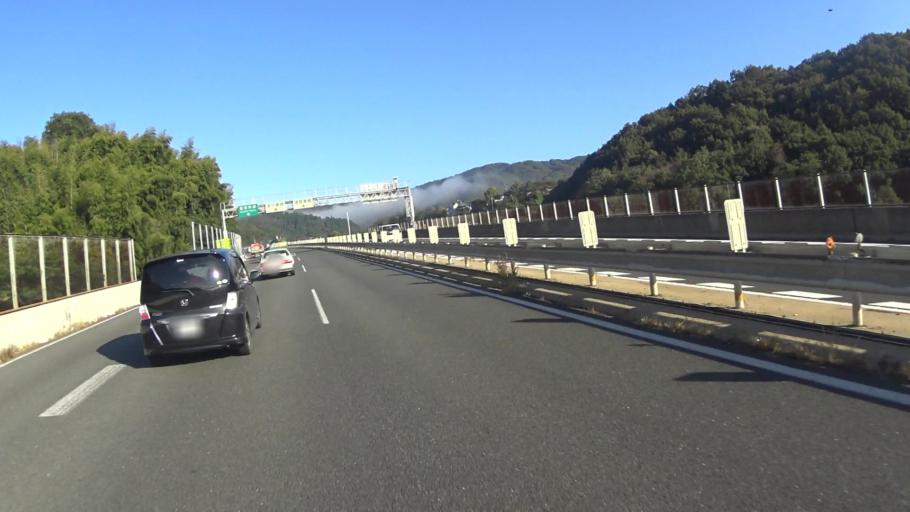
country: JP
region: Kyoto
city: Muko
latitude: 34.9797
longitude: 135.6564
